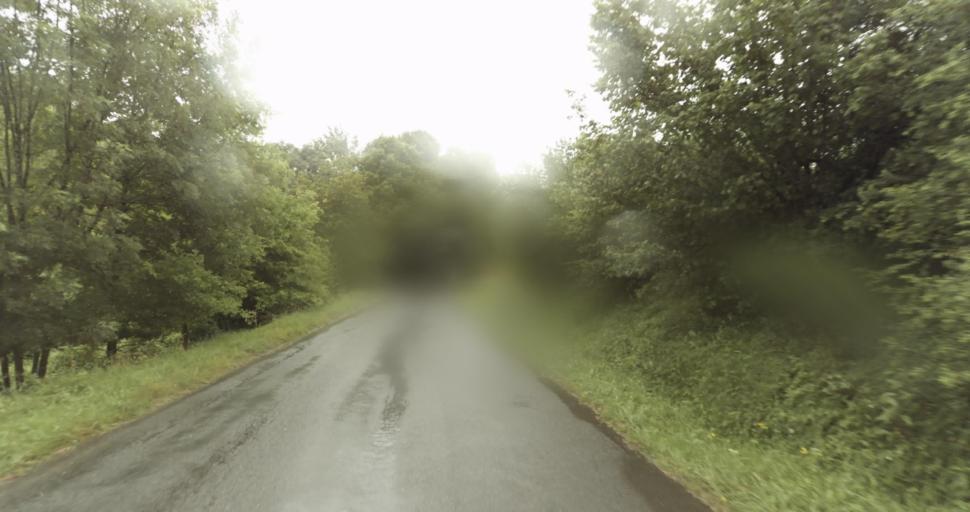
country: FR
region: Aquitaine
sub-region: Departement de la Dordogne
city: Beaumont-du-Perigord
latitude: 44.8122
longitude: 0.8655
